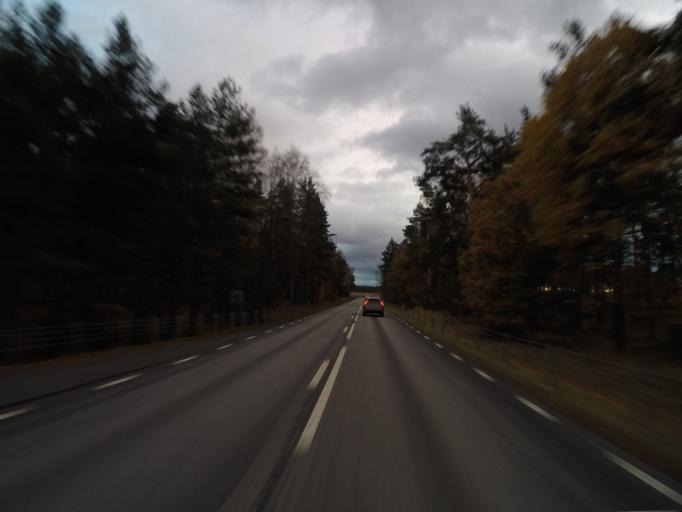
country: SE
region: Skane
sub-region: Kristianstads Kommun
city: Degeberga
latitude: 55.8524
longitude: 14.0945
